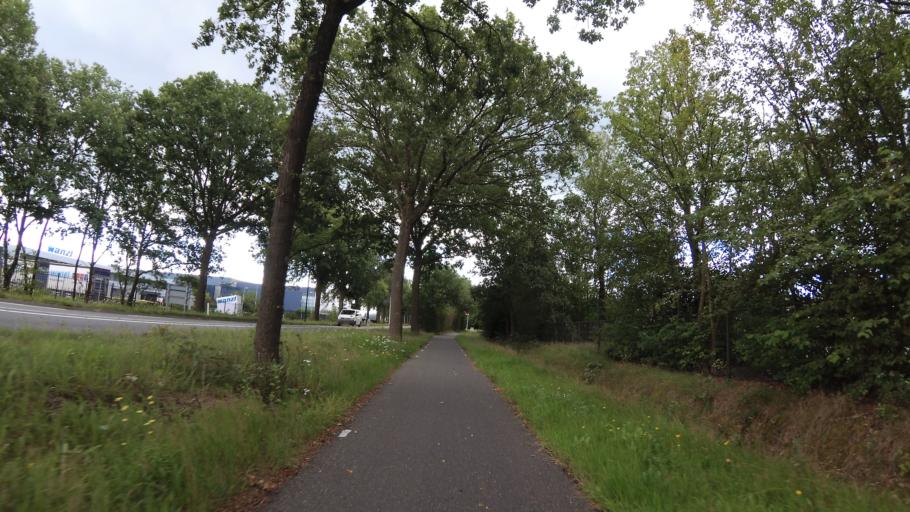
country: NL
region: North Brabant
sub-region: Gemeente Oosterhout
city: Oosterhout
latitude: 51.6212
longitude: 4.8772
